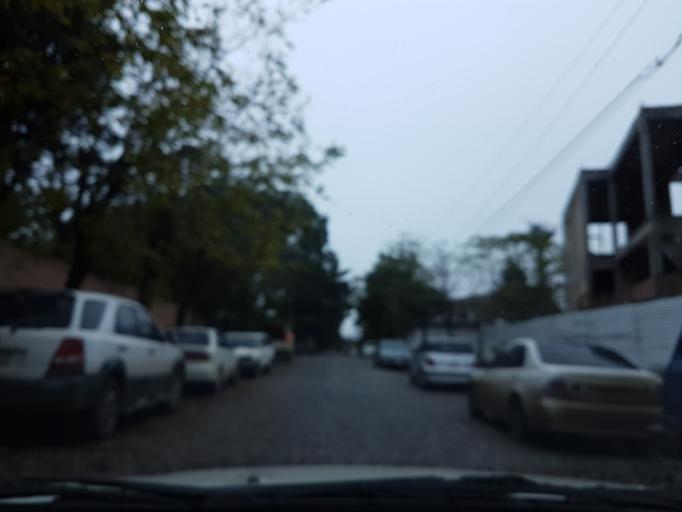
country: PY
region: Central
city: Fernando de la Mora
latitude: -25.2867
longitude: -57.5567
